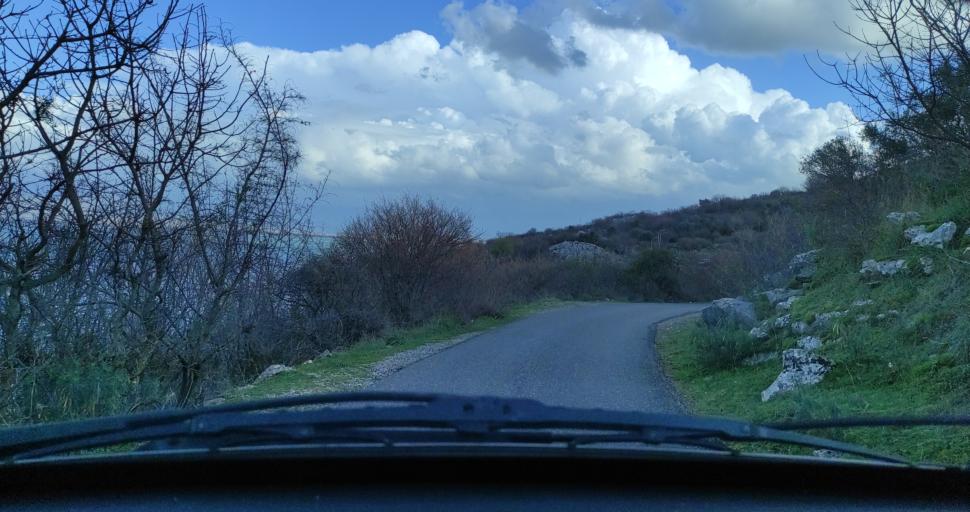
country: AL
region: Shkoder
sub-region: Rrethi i Shkodres
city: Dajc
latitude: 42.0692
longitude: 19.4129
